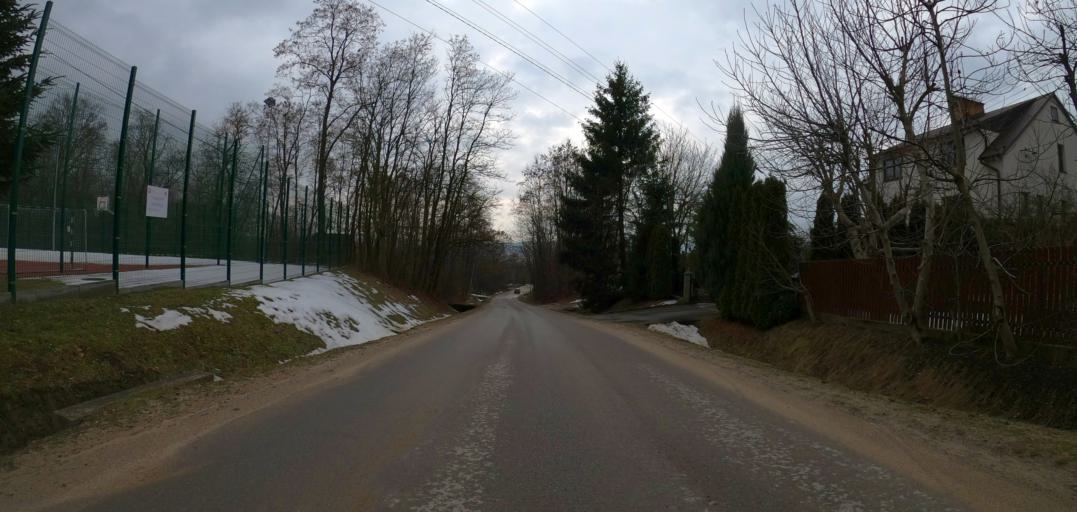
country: PL
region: Subcarpathian Voivodeship
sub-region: Powiat debicki
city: Pilzno
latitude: 49.9834
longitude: 21.3374
